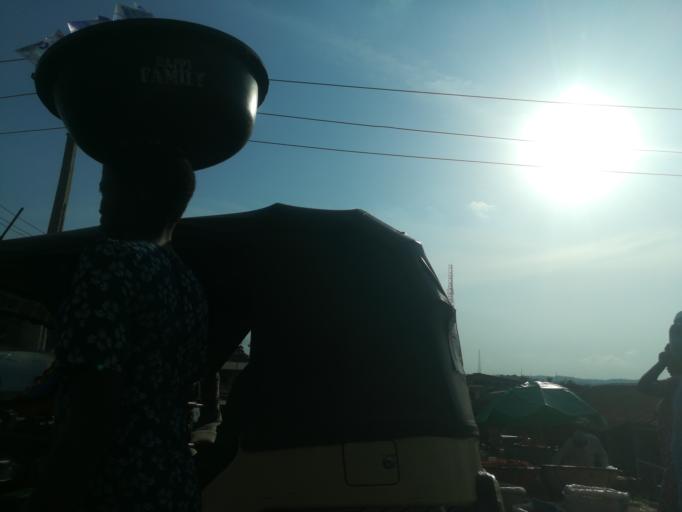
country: NG
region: Oyo
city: Ibadan
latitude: 7.3845
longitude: 3.8258
